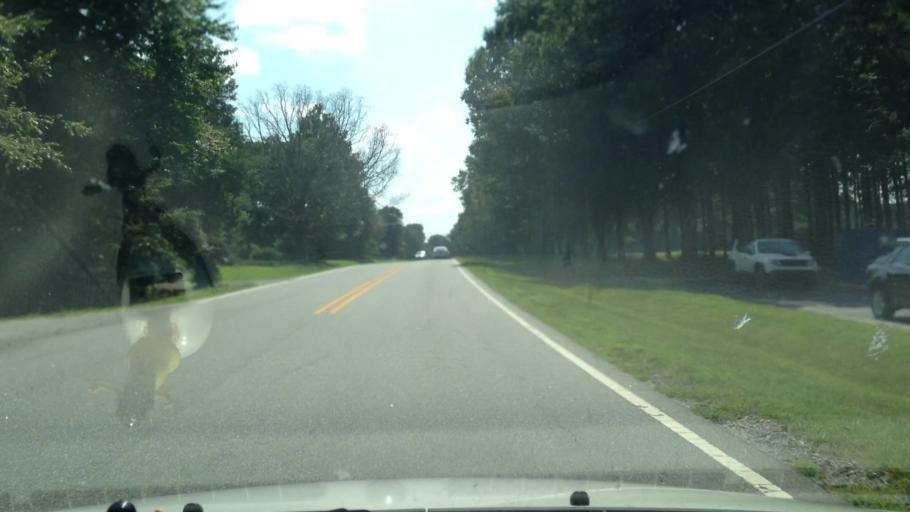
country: US
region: North Carolina
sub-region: Guilford County
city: Oak Ridge
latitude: 36.1683
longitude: -79.9960
